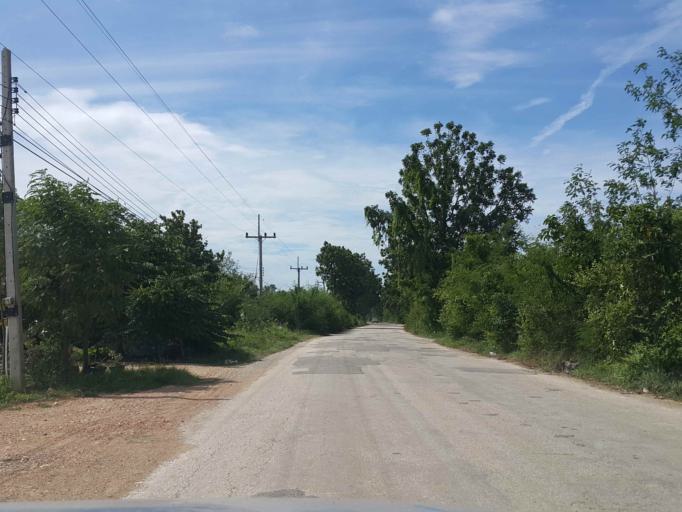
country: TH
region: Sukhothai
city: Ban Dan Lan Hoi
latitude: 17.1433
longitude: 99.5231
